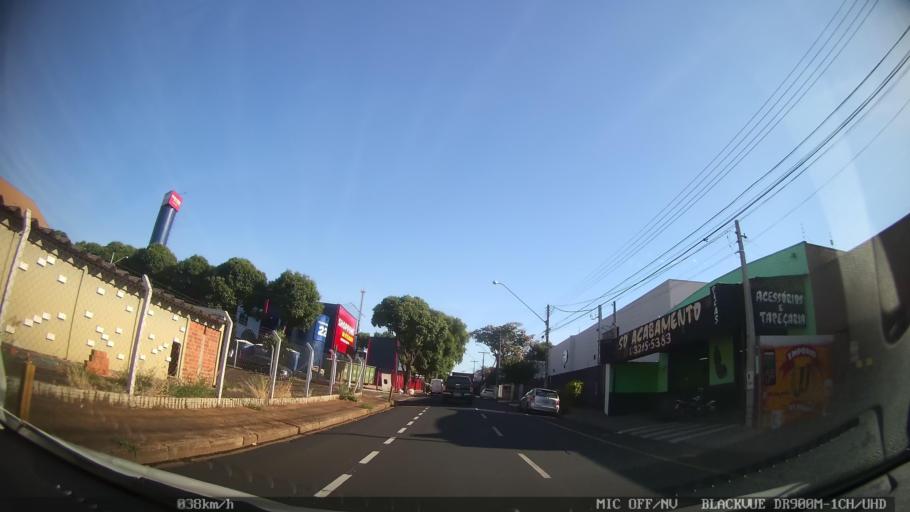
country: BR
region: Sao Paulo
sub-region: Sao Jose Do Rio Preto
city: Sao Jose do Rio Preto
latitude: -20.7873
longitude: -49.3567
